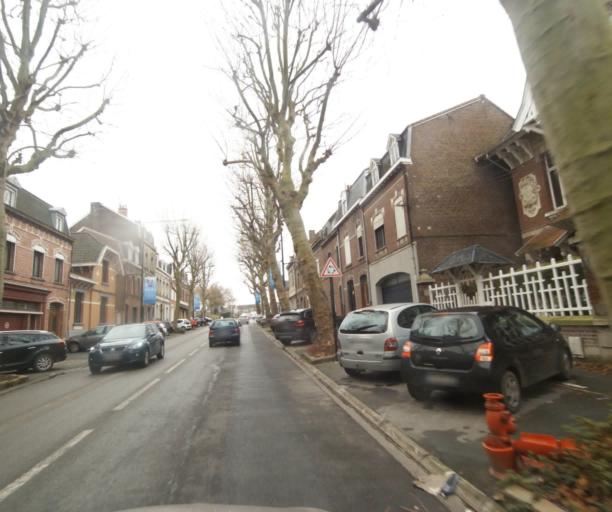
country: FR
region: Nord-Pas-de-Calais
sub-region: Departement du Nord
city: Valenciennes
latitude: 50.3506
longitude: 3.5241
